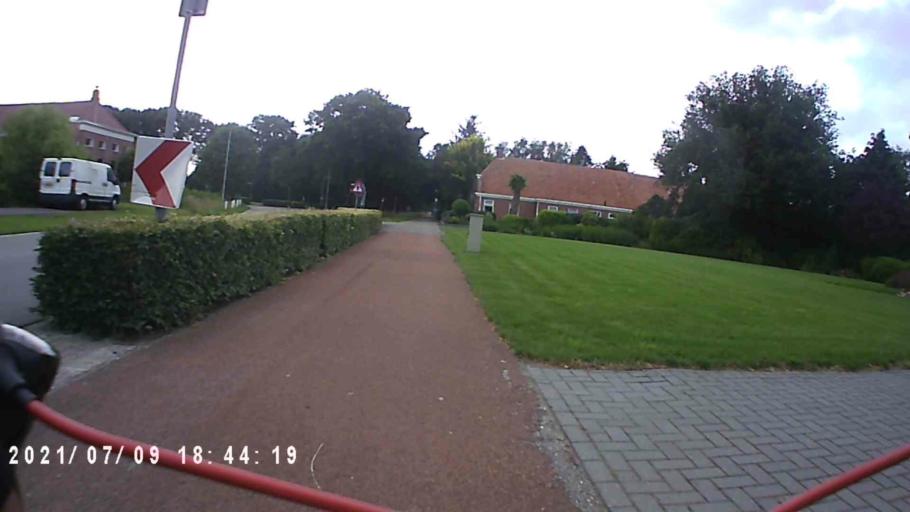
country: NL
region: Groningen
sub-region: Gemeente Veendam
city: Veendam
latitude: 53.0815
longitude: 6.9167
